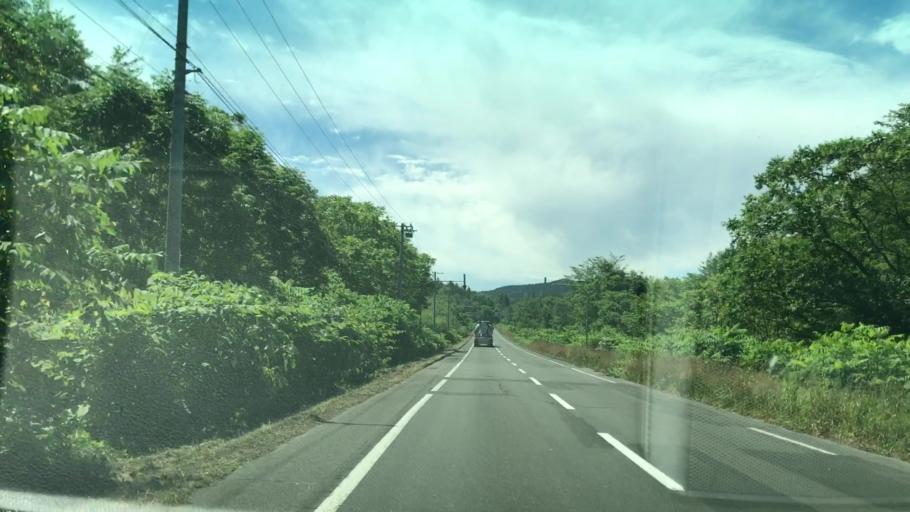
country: JP
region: Hokkaido
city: Shimo-furano
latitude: 42.9386
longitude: 142.4449
